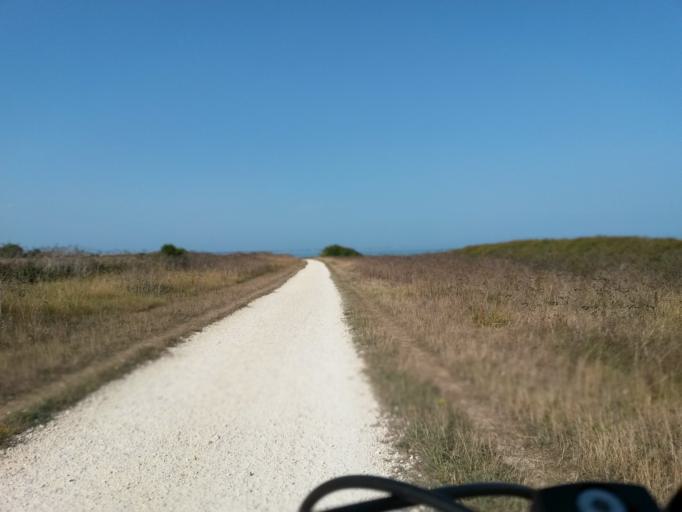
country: FR
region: Poitou-Charentes
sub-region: Departement de la Charente-Maritime
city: Nieul-sur-Mer
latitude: 46.2159
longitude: -1.1899
